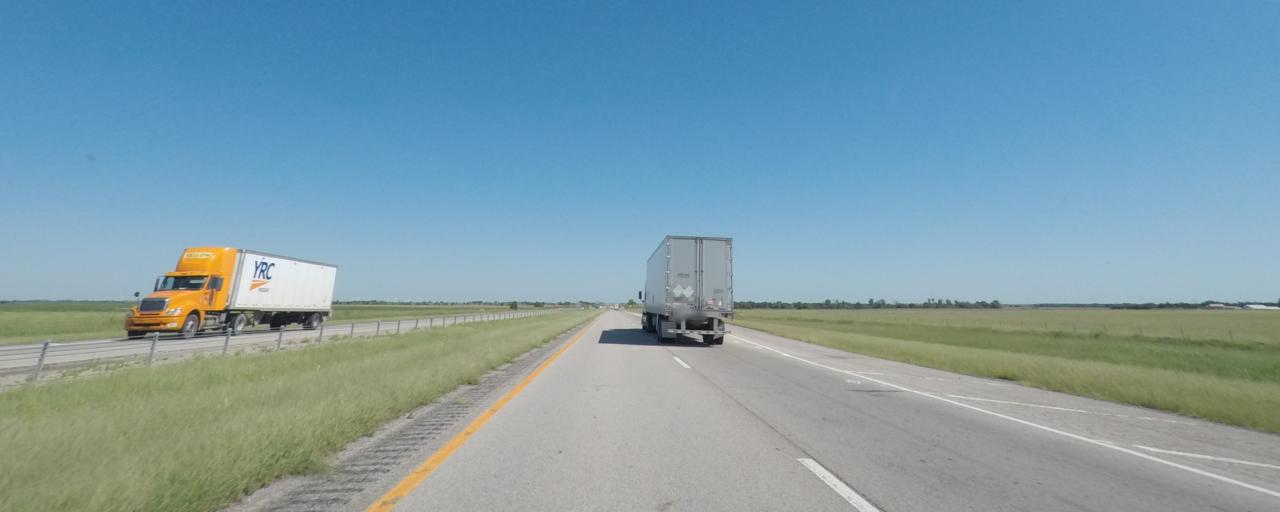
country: US
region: Oklahoma
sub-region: Kay County
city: Tonkawa
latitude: 36.7140
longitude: -97.3458
